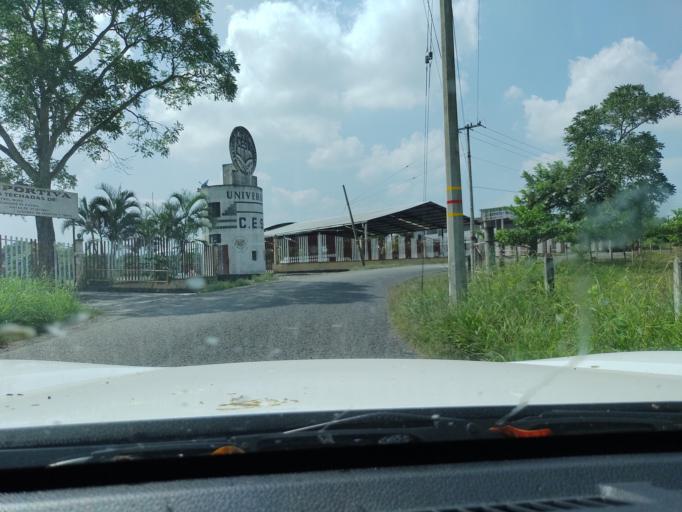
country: MX
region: Veracruz
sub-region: Atzalan
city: Colonias Pedernales
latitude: 20.0622
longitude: -97.0262
